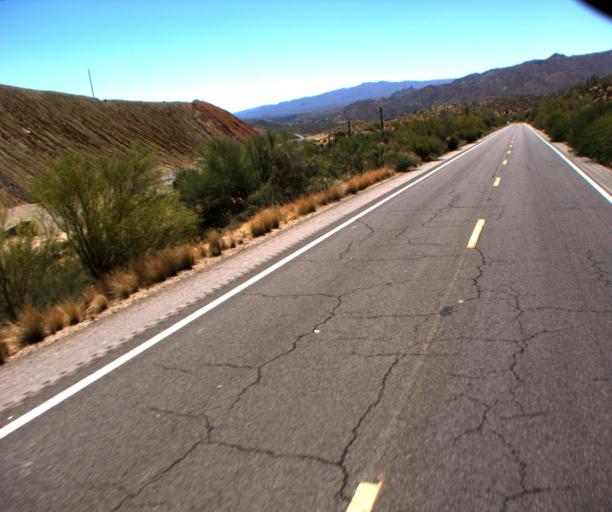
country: US
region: Arizona
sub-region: Pinal County
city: Kearny
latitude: 33.1418
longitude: -110.9910
